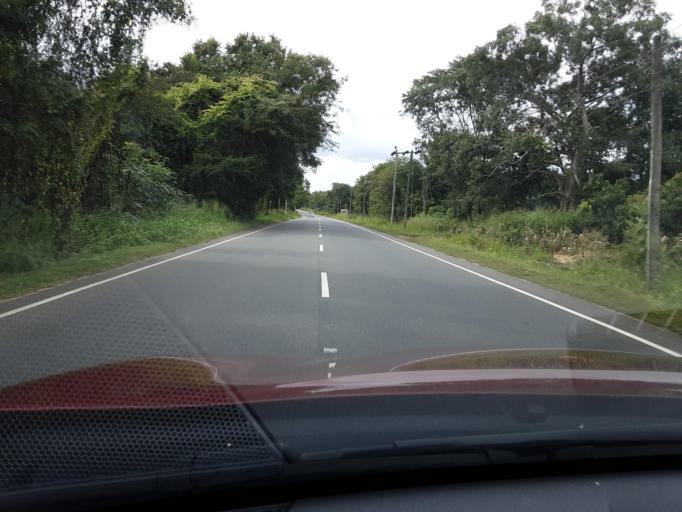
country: LK
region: Uva
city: Badulla
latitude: 7.3949
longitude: 81.1263
